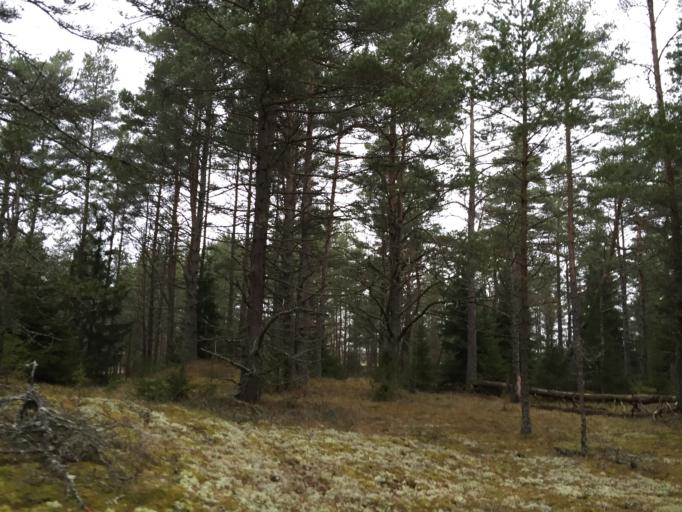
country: EE
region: Saare
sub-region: Kuressaare linn
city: Kuressaare
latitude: 58.5029
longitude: 22.3429
